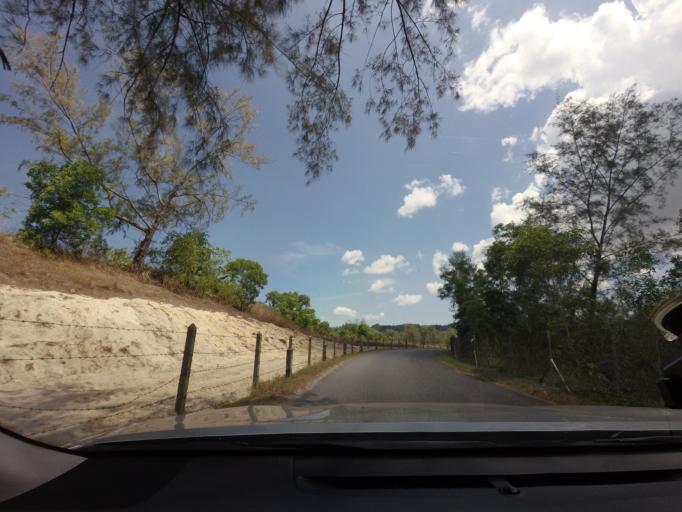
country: TH
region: Phuket
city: Thalang
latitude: 8.0335
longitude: 98.2888
